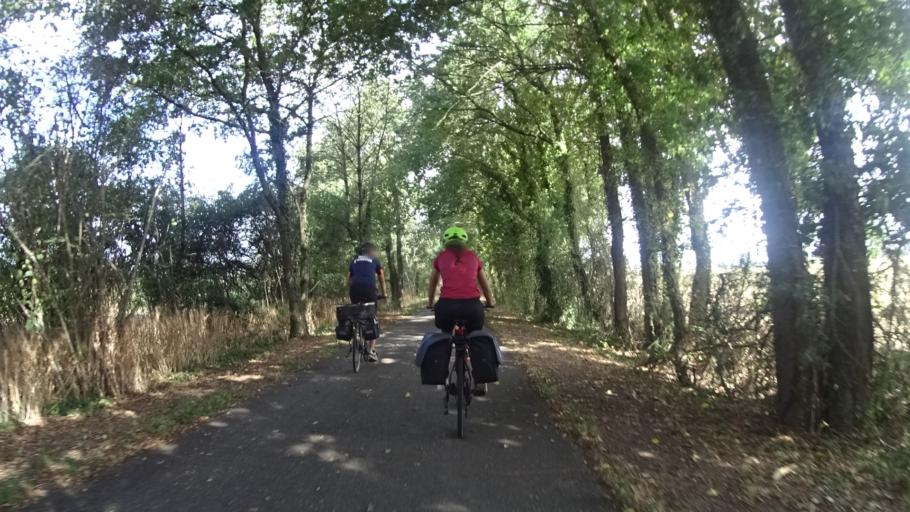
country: FR
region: Bourgogne
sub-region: Departement de Saone-et-Loire
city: Bourbon-Lancy
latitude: 46.6088
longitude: 3.7444
